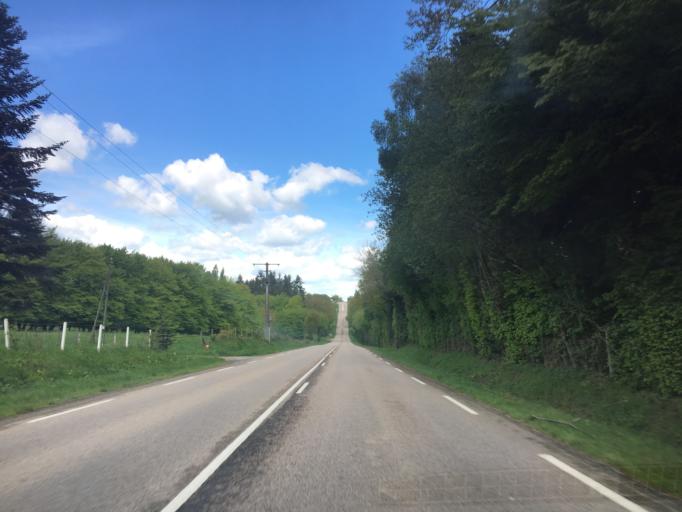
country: FR
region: Lower Normandy
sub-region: Departement de l'Orne
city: Rai
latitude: 48.7847
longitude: 0.6017
